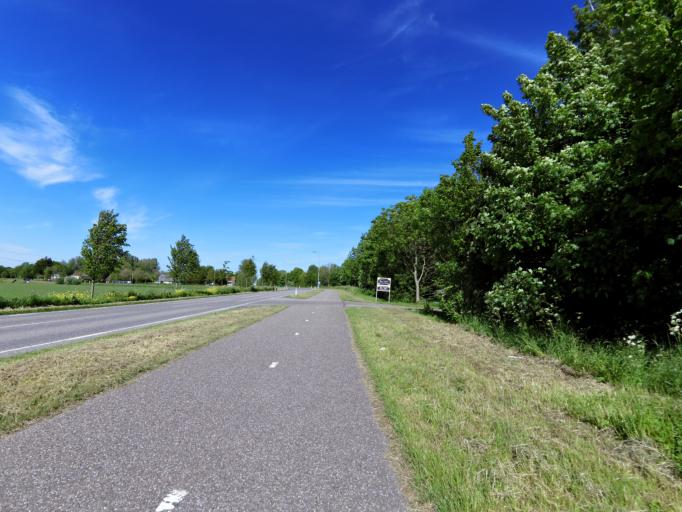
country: NL
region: South Holland
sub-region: Gemeente Brielle
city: Brielle
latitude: 51.8784
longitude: 4.1592
